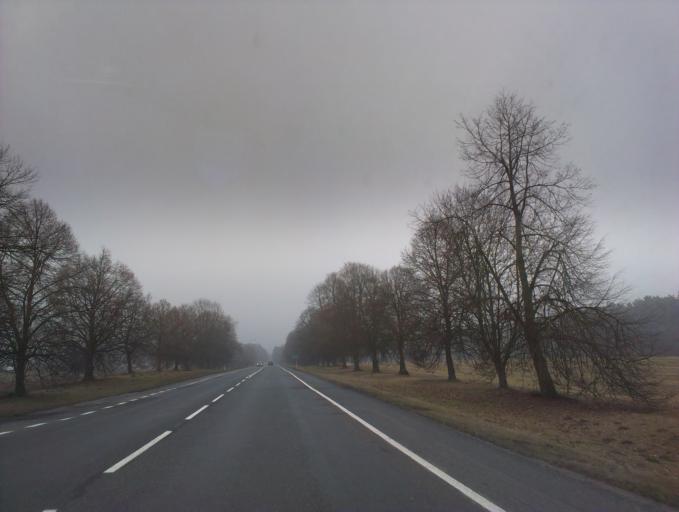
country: PL
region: Greater Poland Voivodeship
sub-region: Powiat chodzieski
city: Chodziez
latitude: 53.0108
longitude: 16.8475
